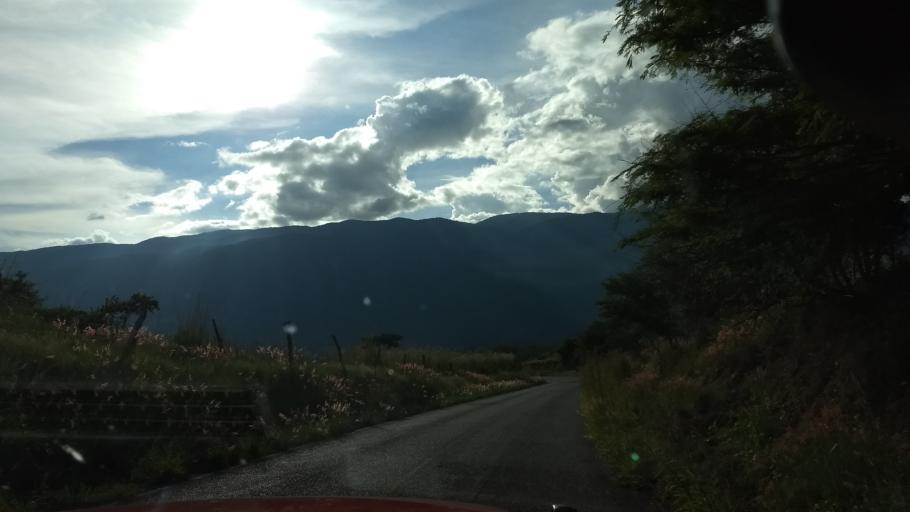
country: MX
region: Colima
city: Suchitlan
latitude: 19.4571
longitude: -103.7996
